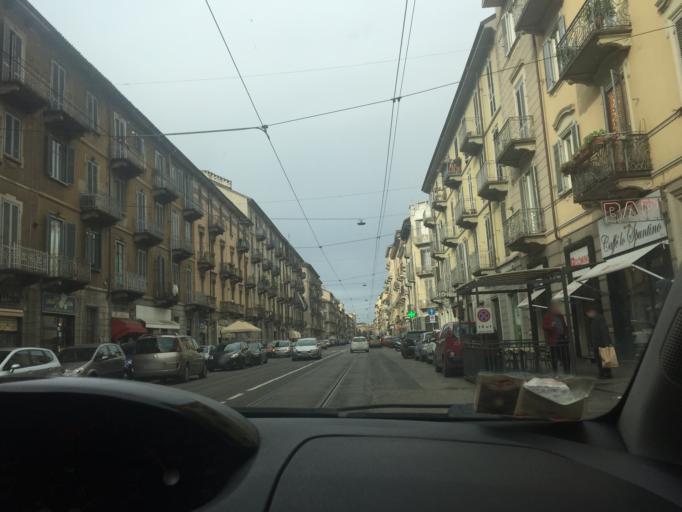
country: IT
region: Piedmont
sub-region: Provincia di Torino
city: Lesna
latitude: 45.0653
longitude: 7.6501
